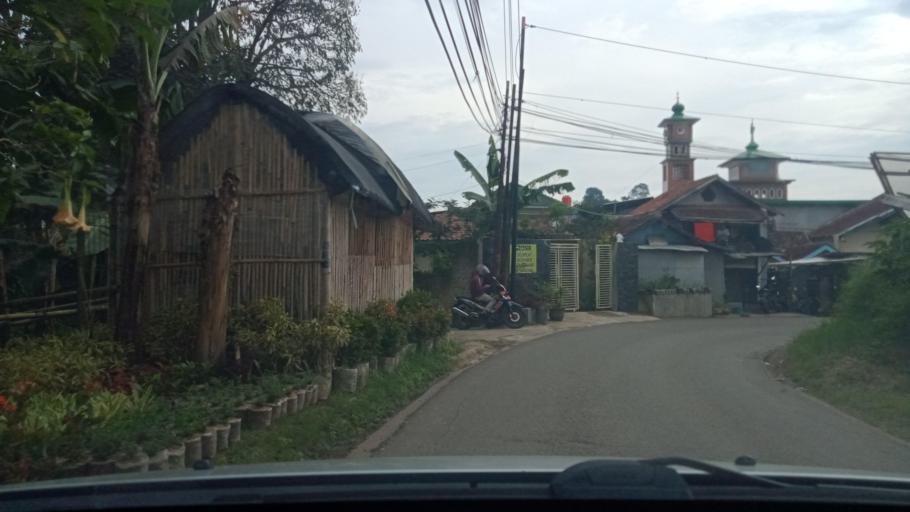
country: ID
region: West Java
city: Lembang
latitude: -6.8151
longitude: 107.5887
